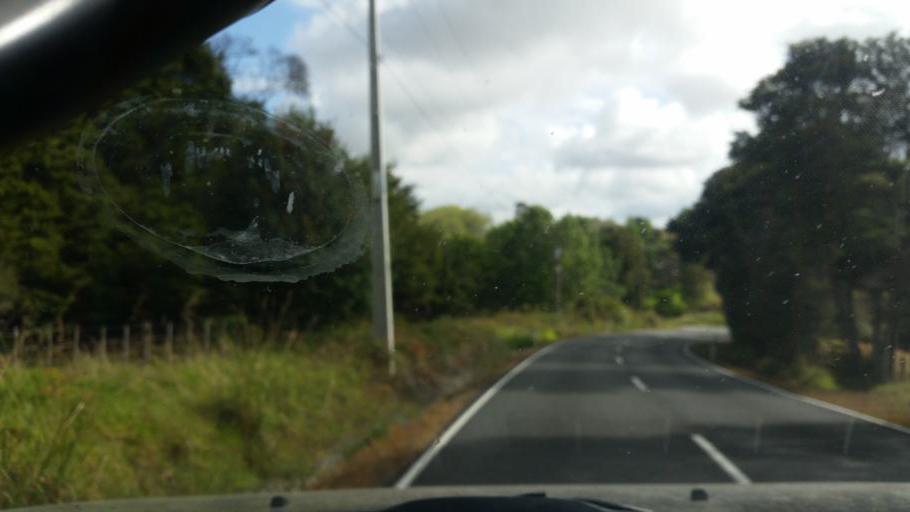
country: NZ
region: Auckland
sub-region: Auckland
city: Wellsford
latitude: -36.1556
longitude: 174.4631
